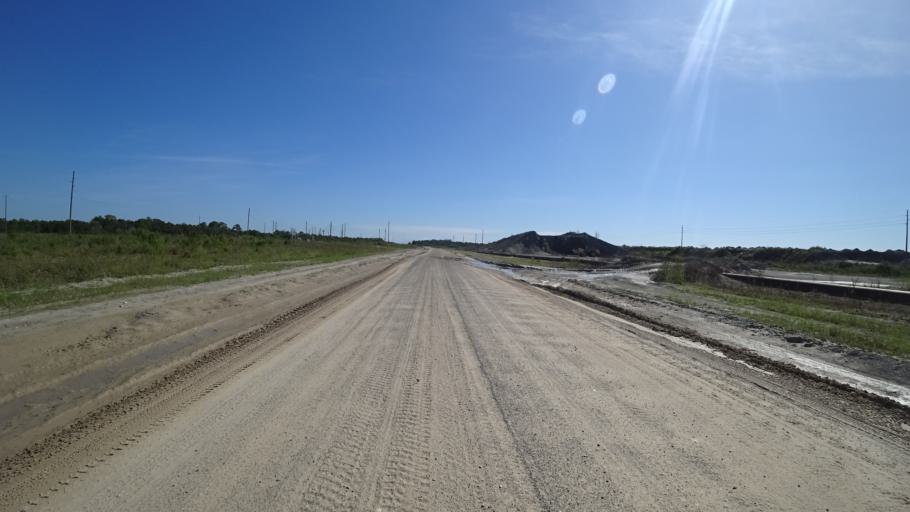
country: US
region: Florida
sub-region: Hillsborough County
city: Balm
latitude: 27.6474
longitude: -82.1135
